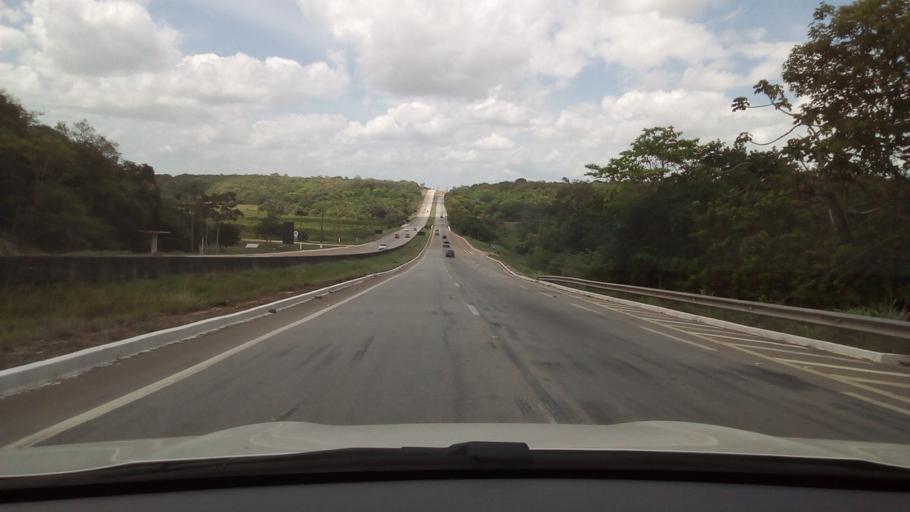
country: BR
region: Paraiba
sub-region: Mamanguape
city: Mamanguape
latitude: -6.9437
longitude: -35.0963
